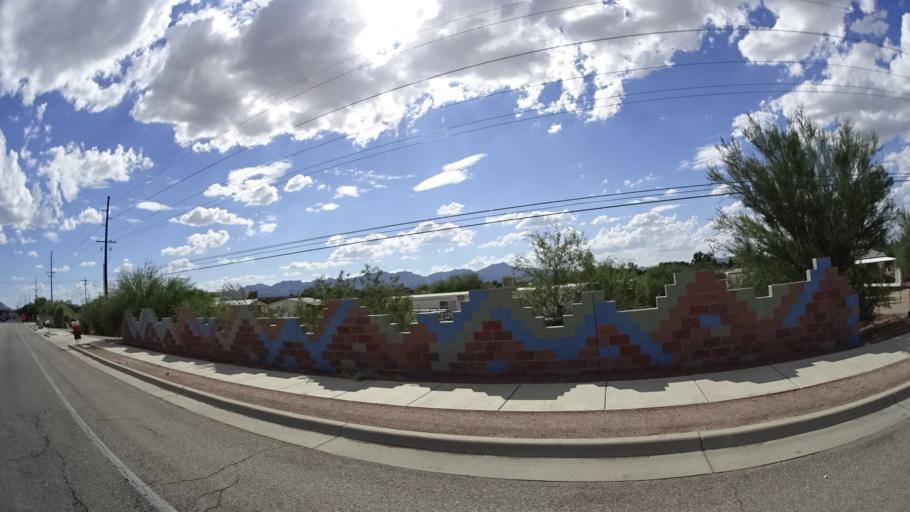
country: US
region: Arizona
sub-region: Pima County
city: Flowing Wells
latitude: 32.3101
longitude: -111.0123
